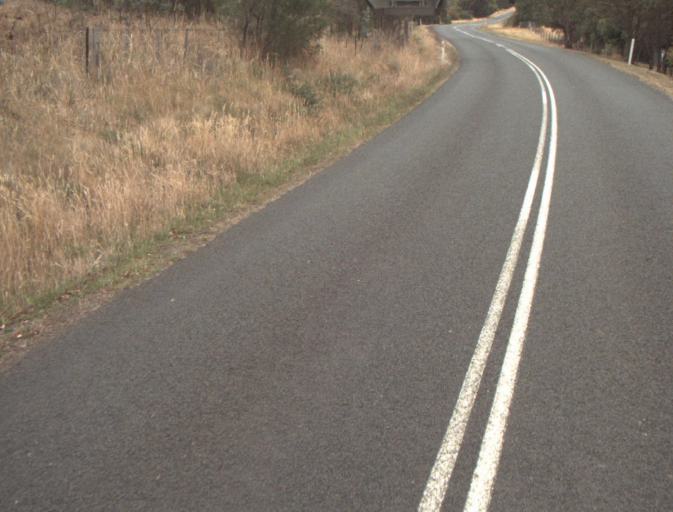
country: AU
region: Tasmania
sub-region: Northern Midlands
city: Evandale
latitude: -41.5143
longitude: 147.2952
